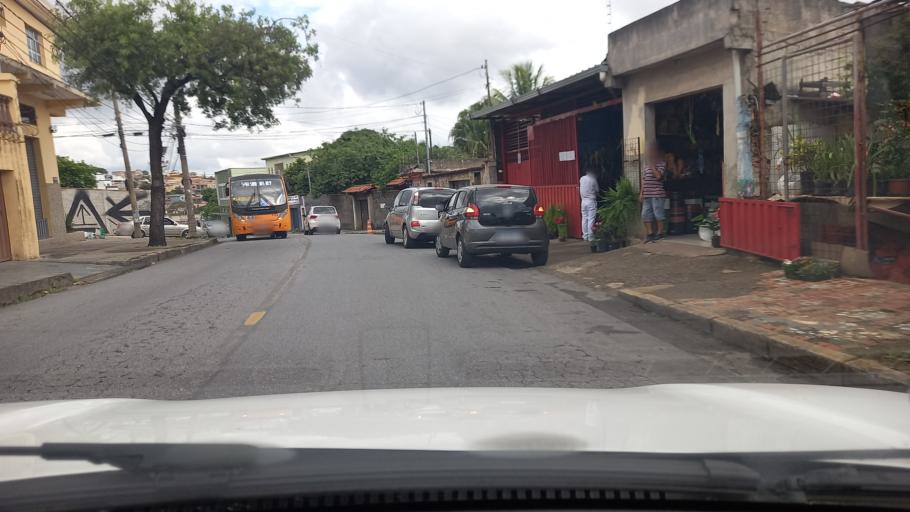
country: BR
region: Minas Gerais
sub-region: Contagem
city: Contagem
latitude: -19.9080
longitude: -44.0047
